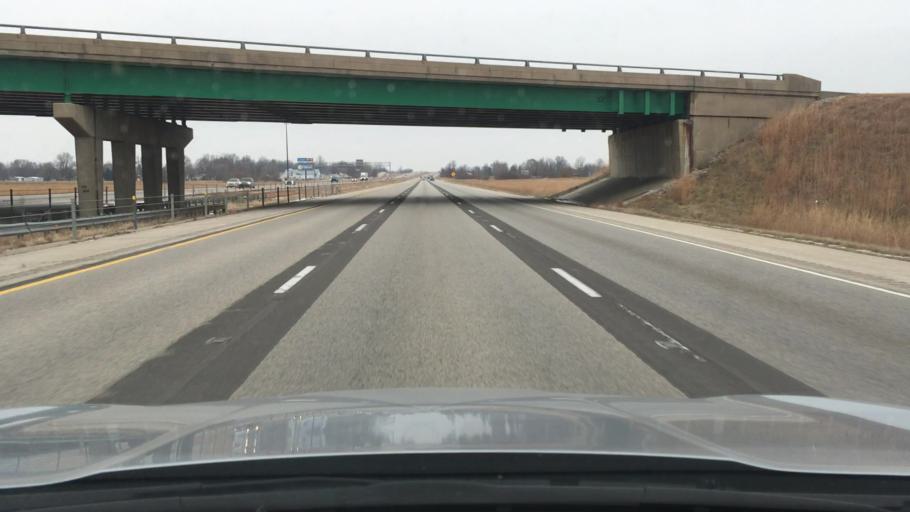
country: US
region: Illinois
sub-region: Sangamon County
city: Divernon
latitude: 39.6160
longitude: -89.6468
